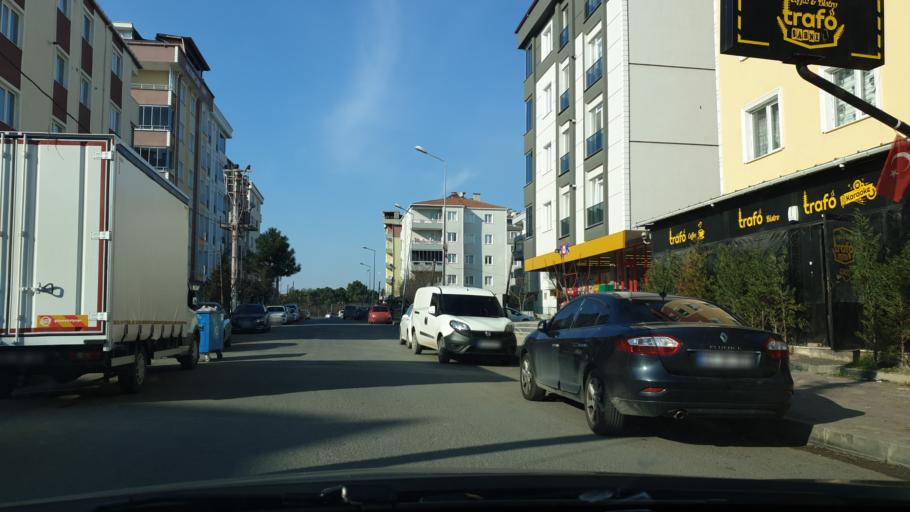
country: TR
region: Tekirdag
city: Cerkezkoey
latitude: 41.2931
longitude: 27.9960
